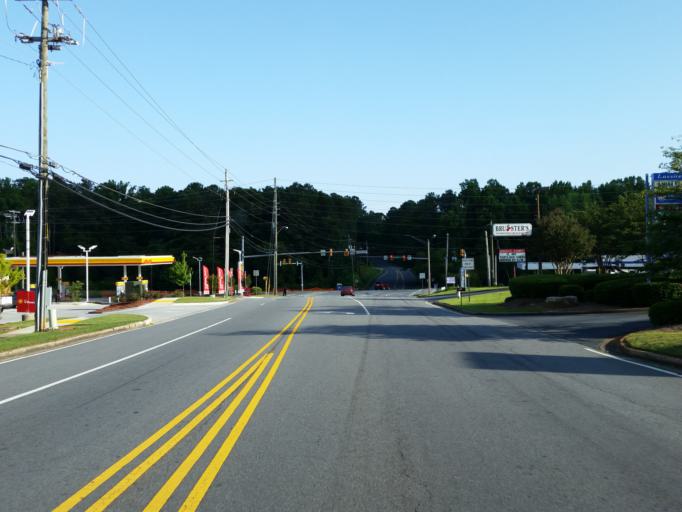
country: US
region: Georgia
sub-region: Cherokee County
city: Woodstock
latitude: 34.0429
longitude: -84.4818
